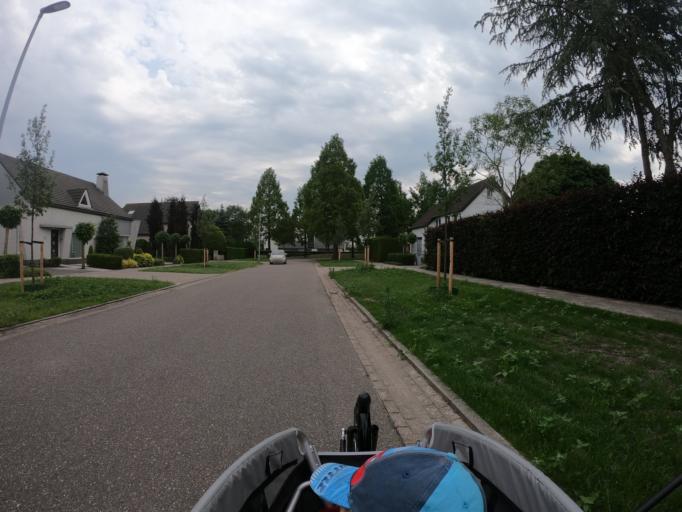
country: NL
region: North Brabant
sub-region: Gemeente Uden
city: Uden
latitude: 51.6501
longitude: 5.6266
